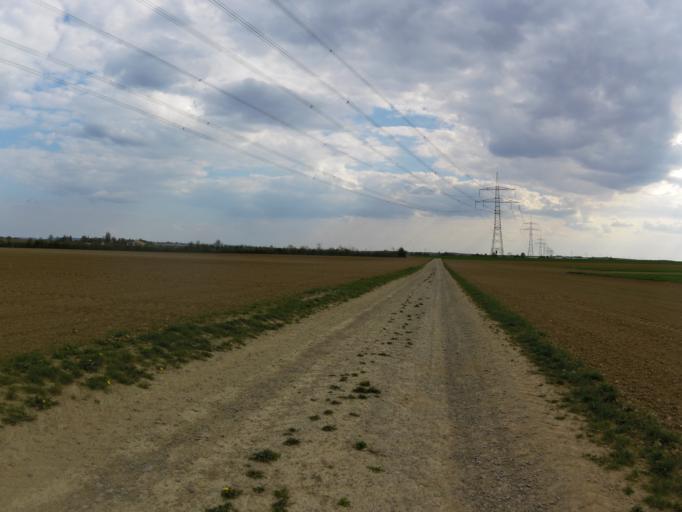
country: DE
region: Bavaria
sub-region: Regierungsbezirk Unterfranken
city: Oberpleichfeld
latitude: 49.8506
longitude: 10.0948
